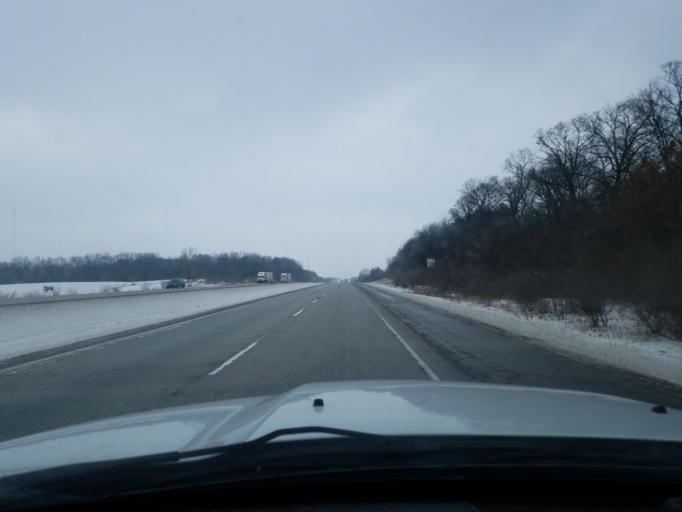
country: US
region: Indiana
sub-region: Fulton County
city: Rochester
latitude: 41.1268
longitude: -86.2397
